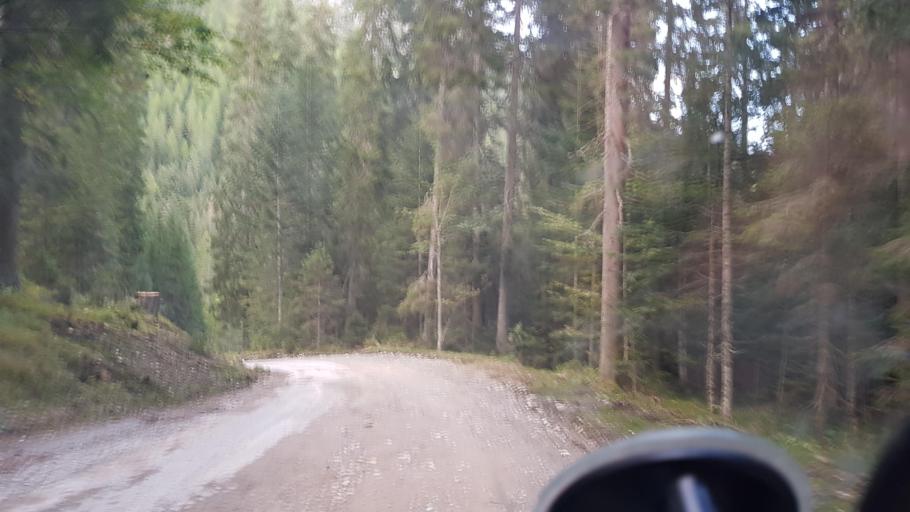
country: IT
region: Veneto
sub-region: Provincia di Belluno
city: San Pietro di Cadore
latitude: 46.6075
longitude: 12.5959
